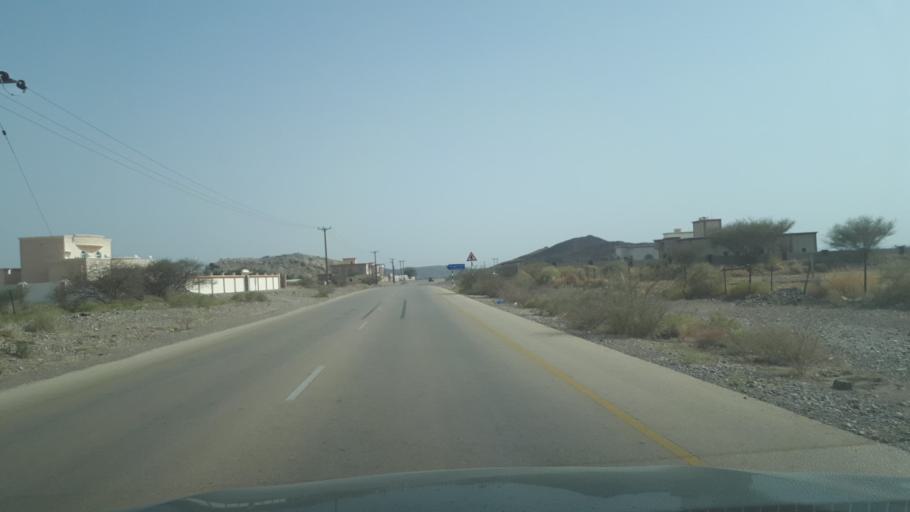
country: OM
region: Az Zahirah
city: `Ibri
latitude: 23.1593
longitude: 56.9119
